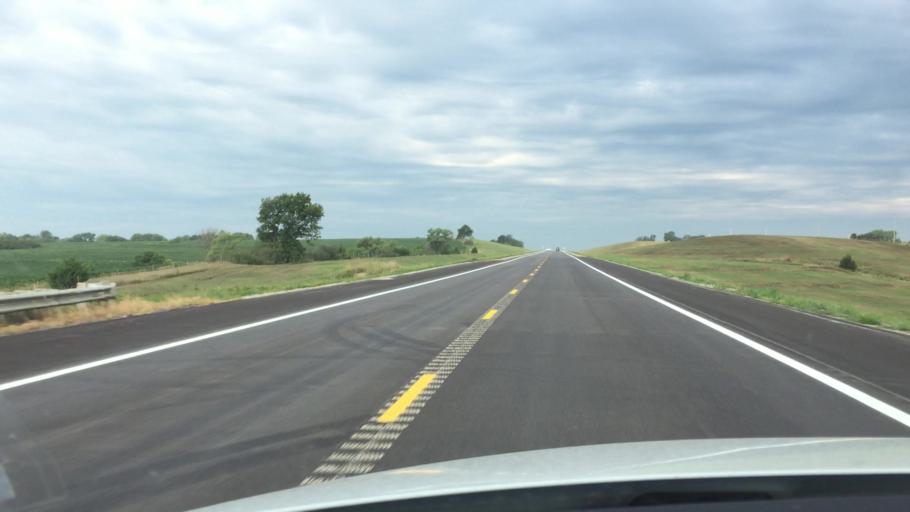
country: US
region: Kansas
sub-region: Doniphan County
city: Highland
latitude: 39.8412
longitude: -95.3789
